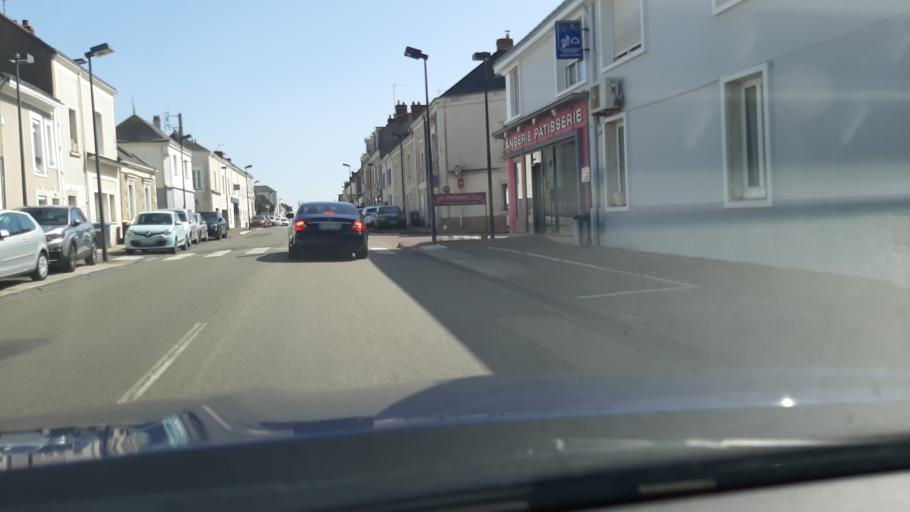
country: FR
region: Pays de la Loire
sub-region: Departement de Maine-et-Loire
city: Trelaze
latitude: 47.4422
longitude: -0.4940
